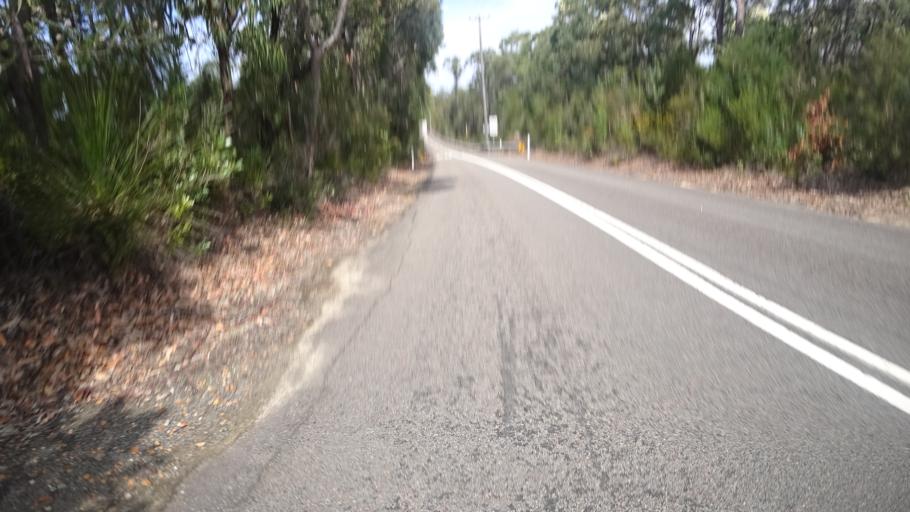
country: AU
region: New South Wales
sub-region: Hornsby Shire
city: Mount Colah
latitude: -33.6682
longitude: 151.1449
